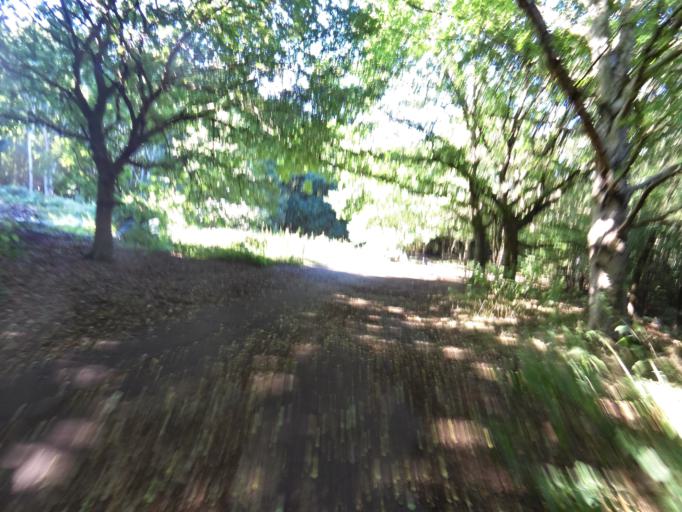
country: GB
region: England
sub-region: Suffolk
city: Kesgrave
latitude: 52.0668
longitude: 1.2653
